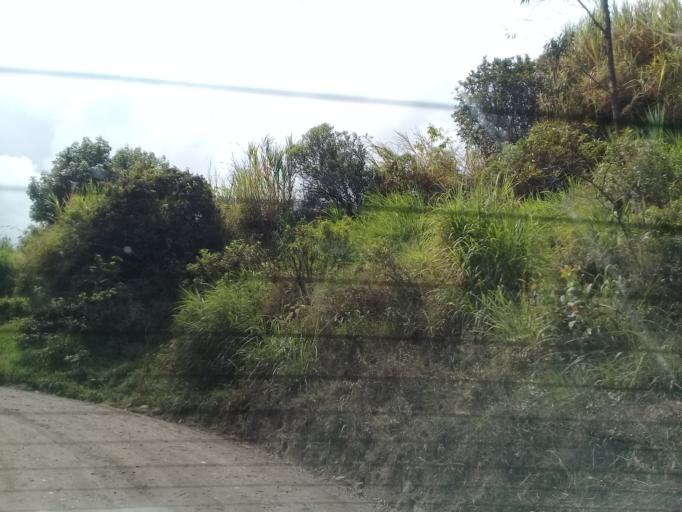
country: CO
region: Cundinamarca
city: Caqueza
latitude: 4.4137
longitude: -73.9857
